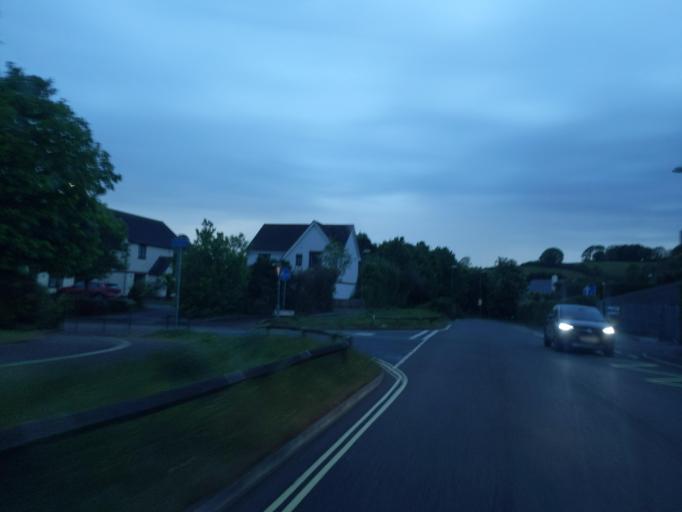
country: GB
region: England
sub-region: Borough of Torbay
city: Paignton
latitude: 50.4275
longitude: -3.5935
